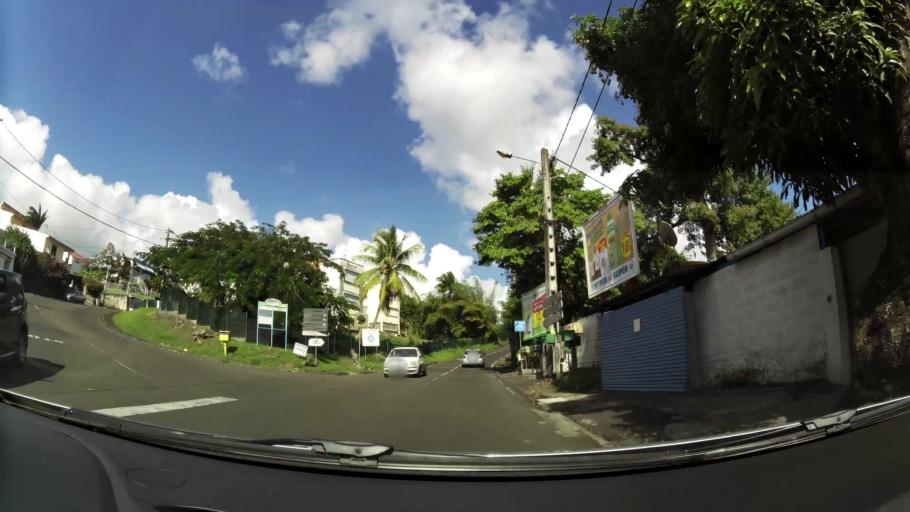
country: MQ
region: Martinique
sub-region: Martinique
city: Fort-de-France
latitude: 14.6181
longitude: -61.0568
